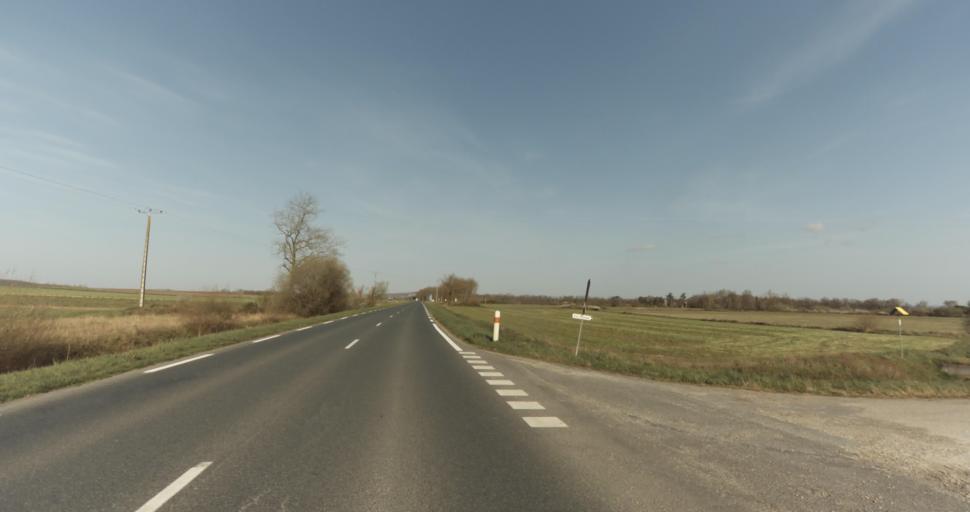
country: FR
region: Midi-Pyrenees
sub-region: Departement du Tarn
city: Saint-Sulpice-la-Pointe
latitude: 43.7526
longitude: 1.7236
